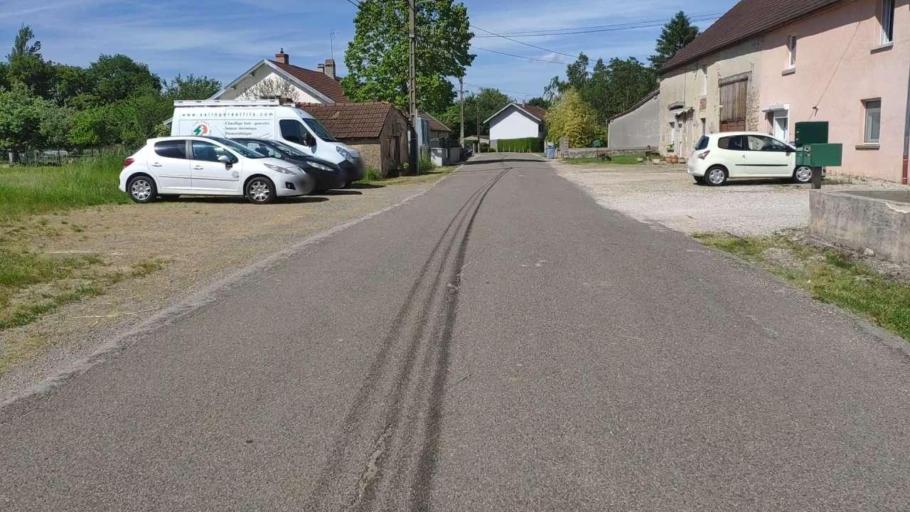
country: FR
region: Franche-Comte
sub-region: Departement du Jura
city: Bletterans
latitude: 46.7668
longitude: 5.4744
